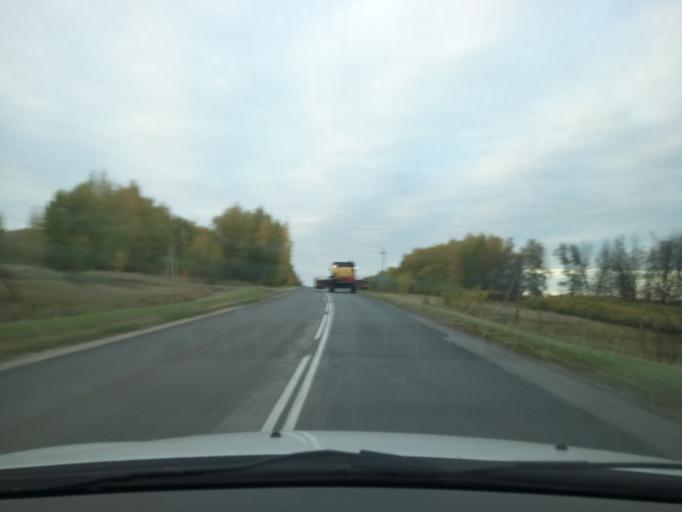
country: RU
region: Nizjnij Novgorod
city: Bol'shoye Murashkino
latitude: 55.7297
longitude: 44.7751
